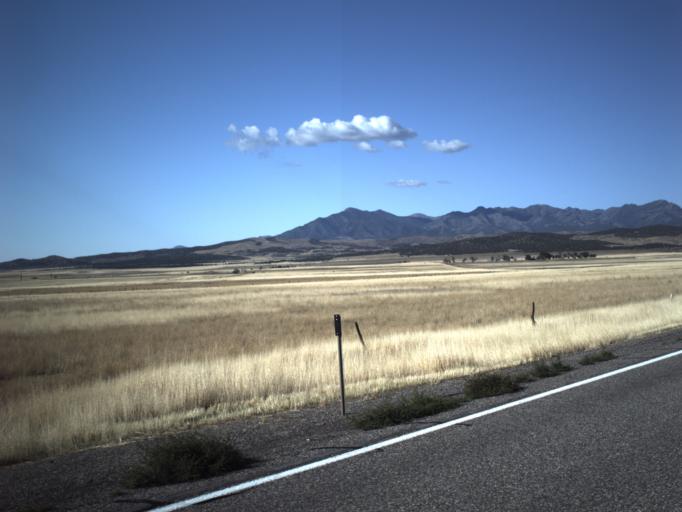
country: US
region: Utah
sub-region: Millard County
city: Fillmore
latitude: 39.1184
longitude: -112.2606
